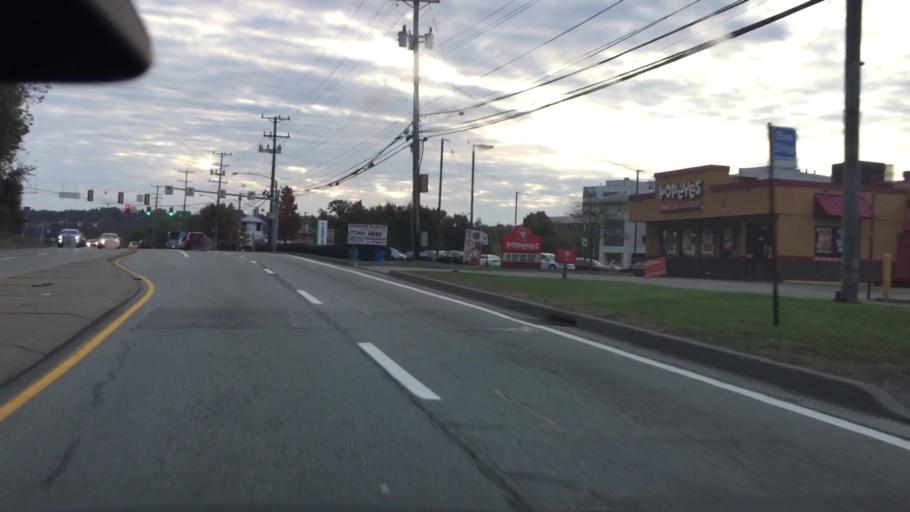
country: US
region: Pennsylvania
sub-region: Allegheny County
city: Turtle Creek
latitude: 40.4304
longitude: -79.8136
